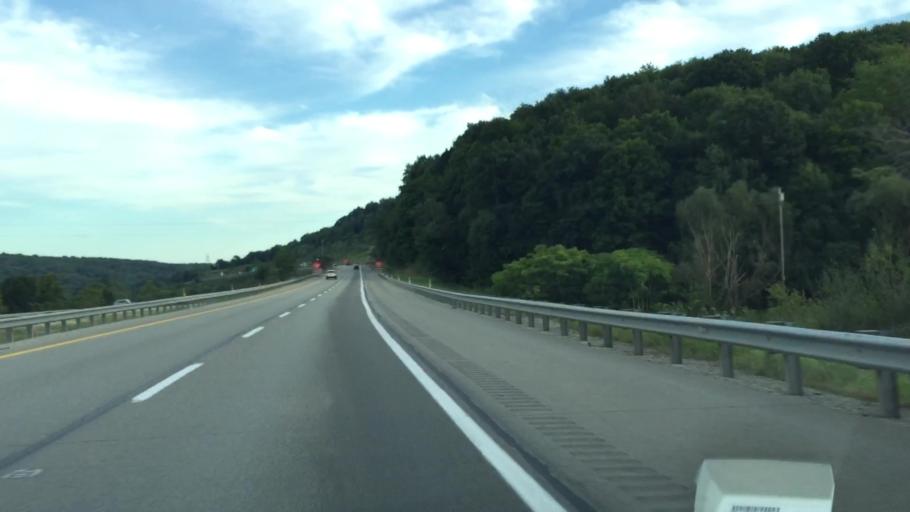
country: US
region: Pennsylvania
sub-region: Allegheny County
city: Ben Avon
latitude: 40.5428
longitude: -80.0822
